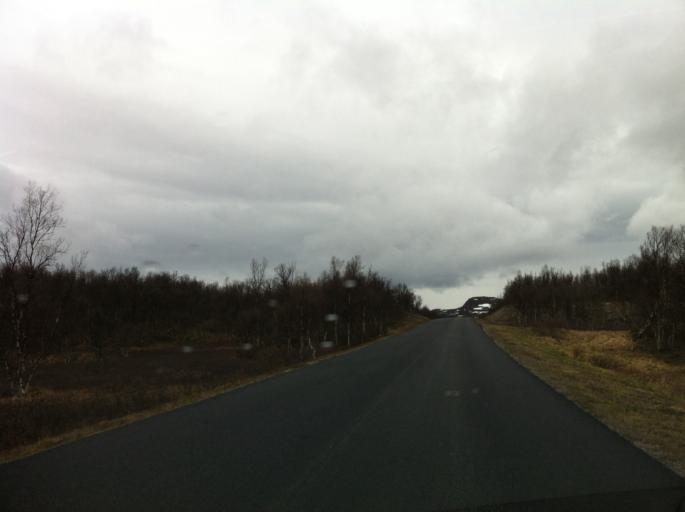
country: NO
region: Sor-Trondelag
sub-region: Tydal
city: Aas
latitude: 62.6410
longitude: 12.0583
